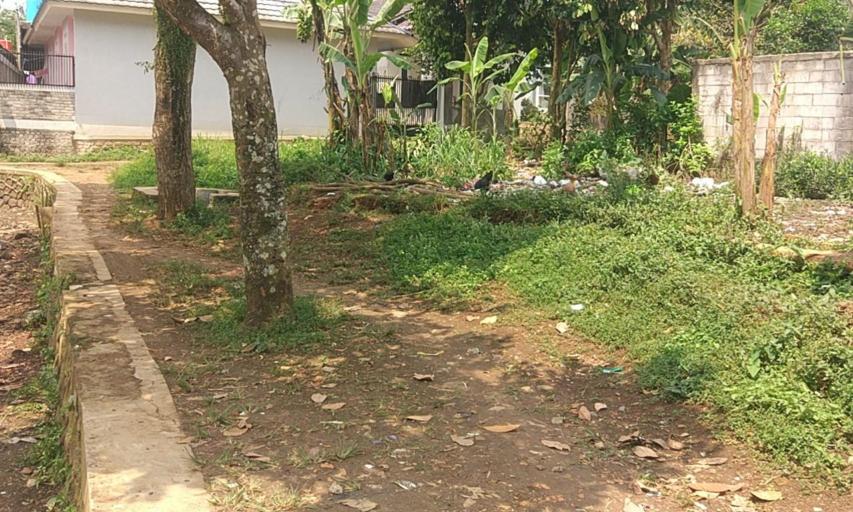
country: ID
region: West Java
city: Ciampea
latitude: -6.5304
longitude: 106.7273
